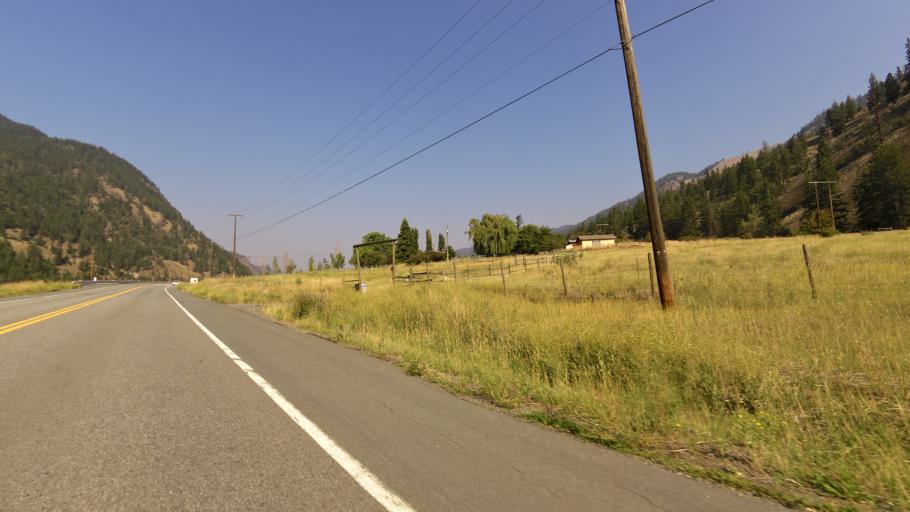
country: CA
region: British Columbia
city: Princeton
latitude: 49.3608
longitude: -120.1100
